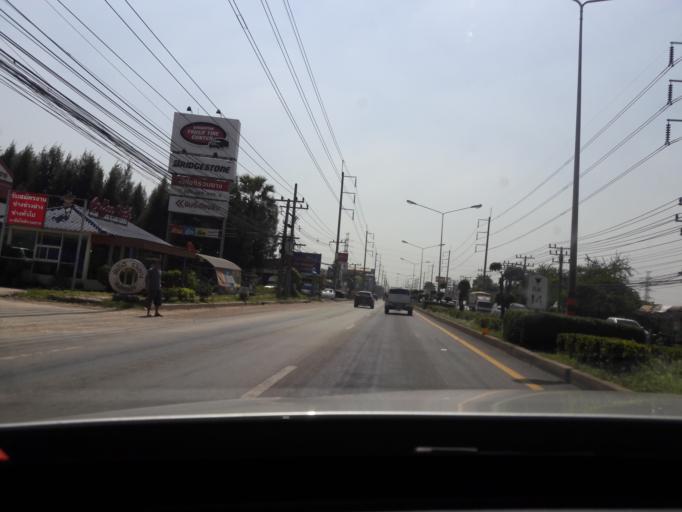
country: TH
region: Samut Sakhon
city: Krathum Baen
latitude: 13.6084
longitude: 100.2870
